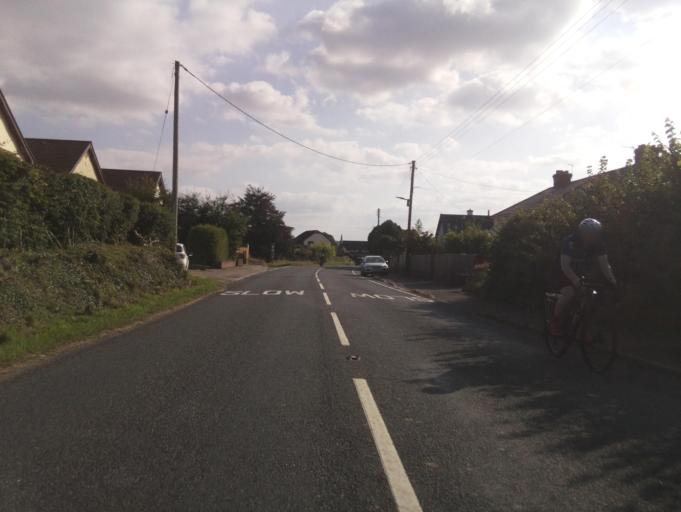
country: GB
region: England
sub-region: Devon
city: Heavitree
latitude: 50.7884
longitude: -3.4943
